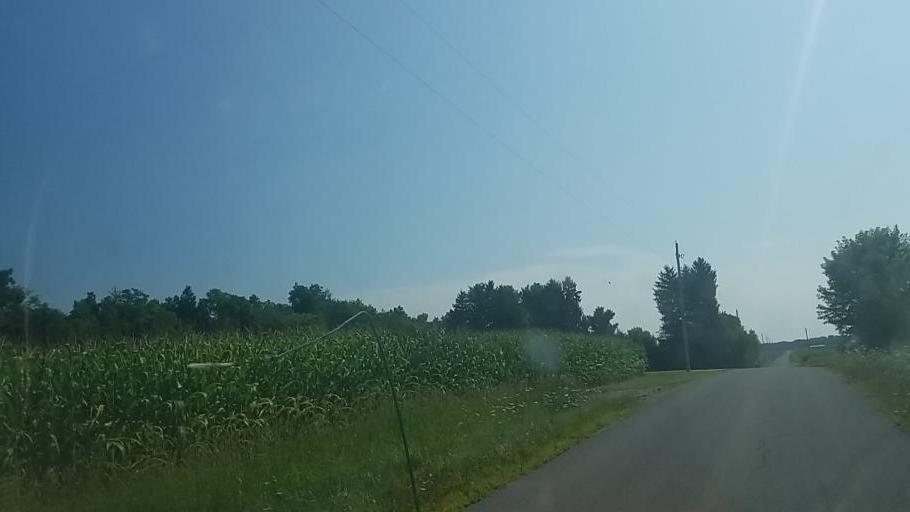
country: US
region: Ohio
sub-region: Marion County
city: Marion
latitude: 40.7169
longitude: -83.1631
